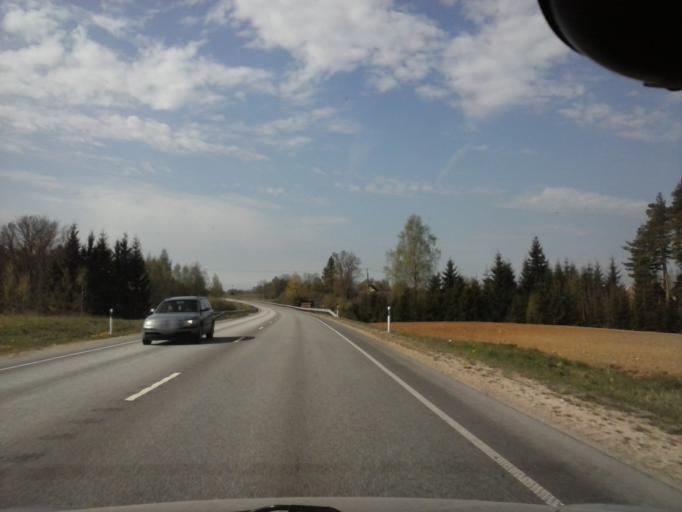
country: EE
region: Tartu
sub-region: UElenurme vald
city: Ulenurme
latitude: 58.1943
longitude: 26.6987
